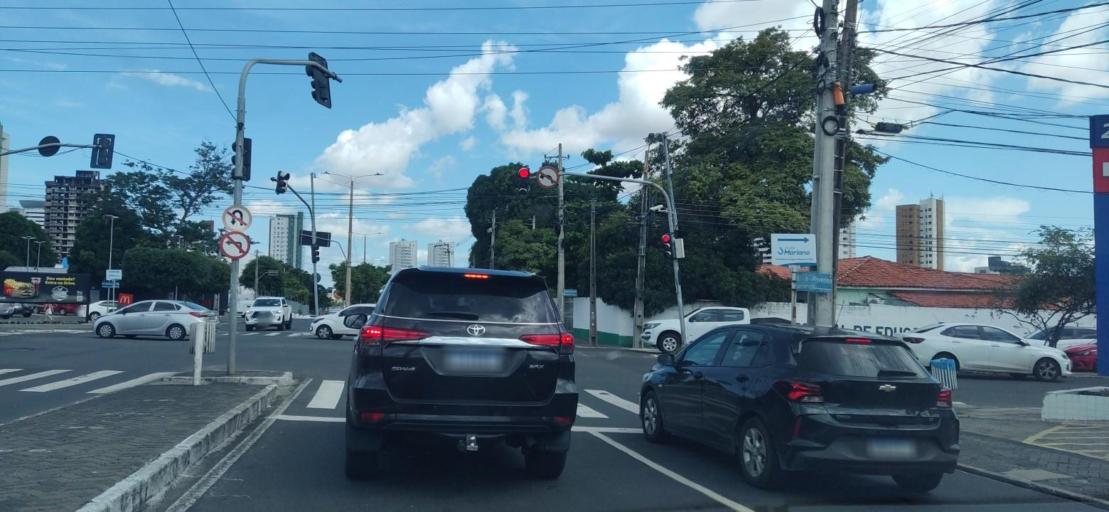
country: BR
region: Piaui
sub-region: Teresina
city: Teresina
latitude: -5.0697
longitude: -42.7926
